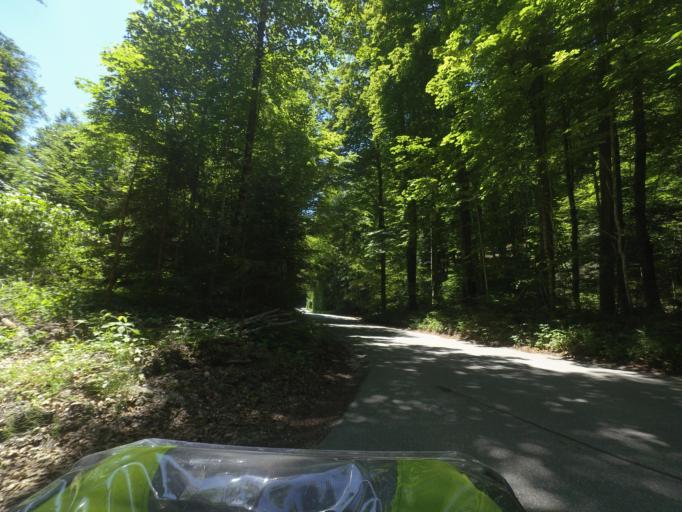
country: AT
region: Salzburg
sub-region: Politischer Bezirk Hallein
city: Oberalm
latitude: 47.7044
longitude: 13.1165
